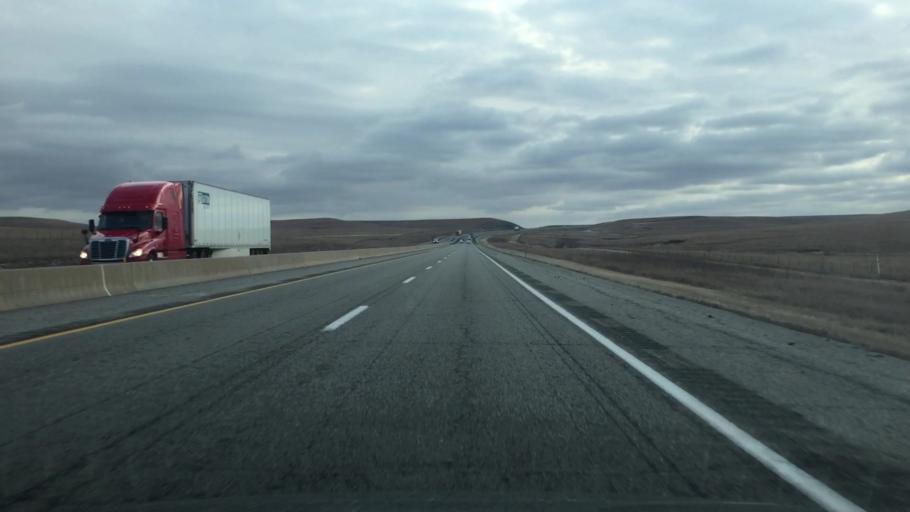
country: US
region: Kansas
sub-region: Chase County
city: Cottonwood Falls
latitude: 38.2493
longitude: -96.3935
